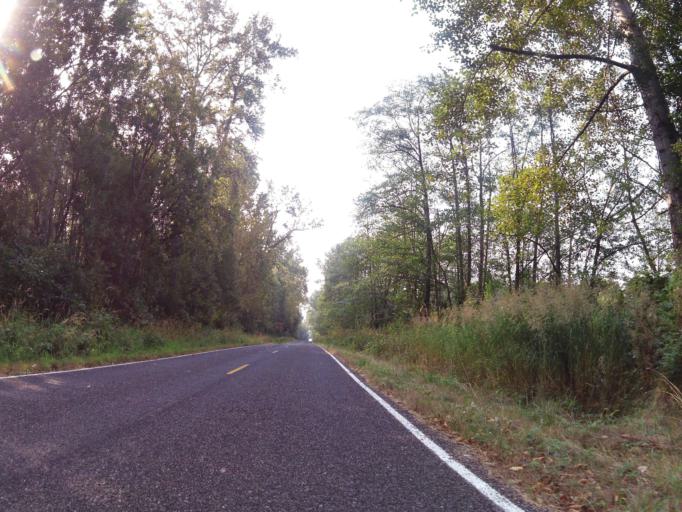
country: US
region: Washington
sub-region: Whatcom County
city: Birch Bay
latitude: 48.8659
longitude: -122.7318
